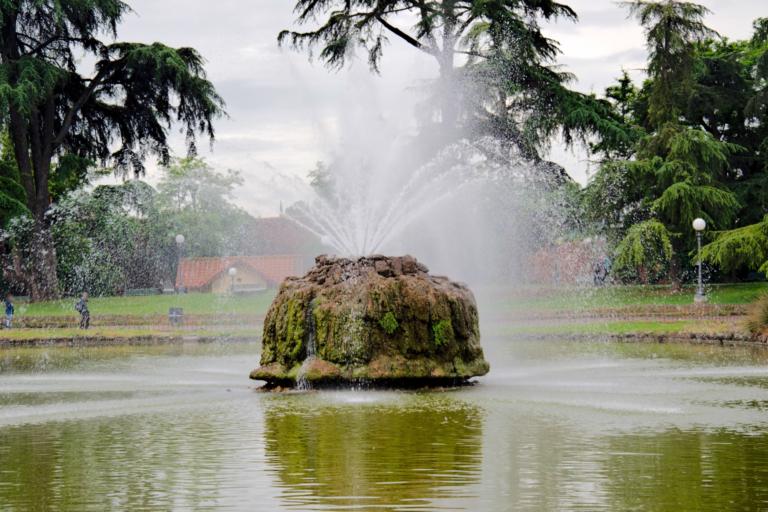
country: IT
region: Tuscany
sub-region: Province of Florence
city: Florence
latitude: 43.7819
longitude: 11.2512
